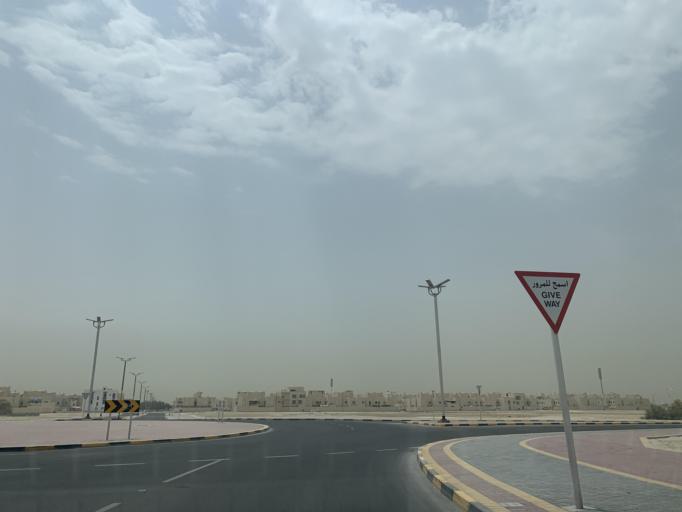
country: BH
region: Northern
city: Madinat `Isa
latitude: 26.1741
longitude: 50.5165
